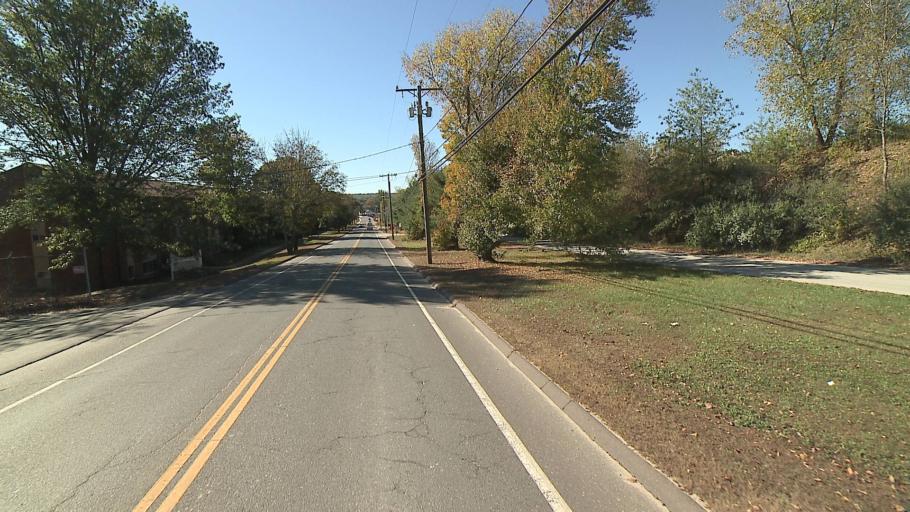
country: US
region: Connecticut
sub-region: Windham County
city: Willimantic
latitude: 41.7236
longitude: -72.1925
